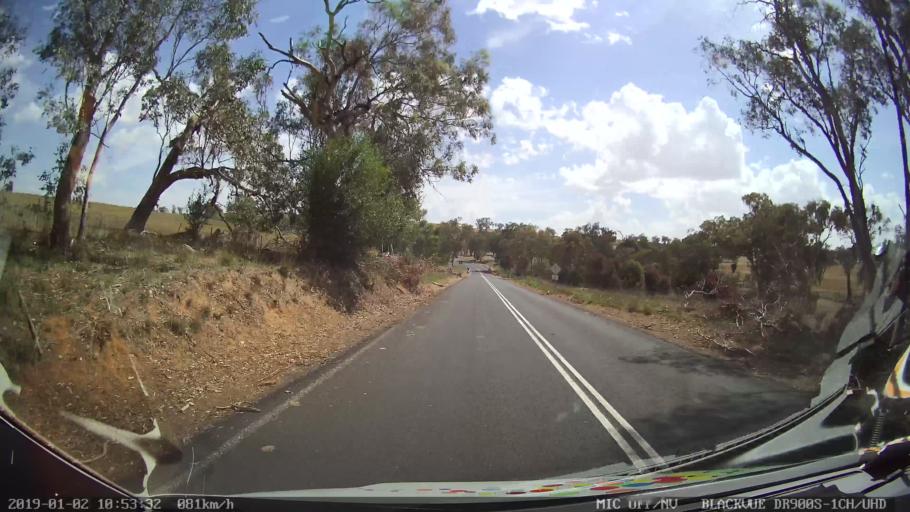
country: AU
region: New South Wales
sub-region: Cootamundra
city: Cootamundra
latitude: -34.6774
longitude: 148.2769
